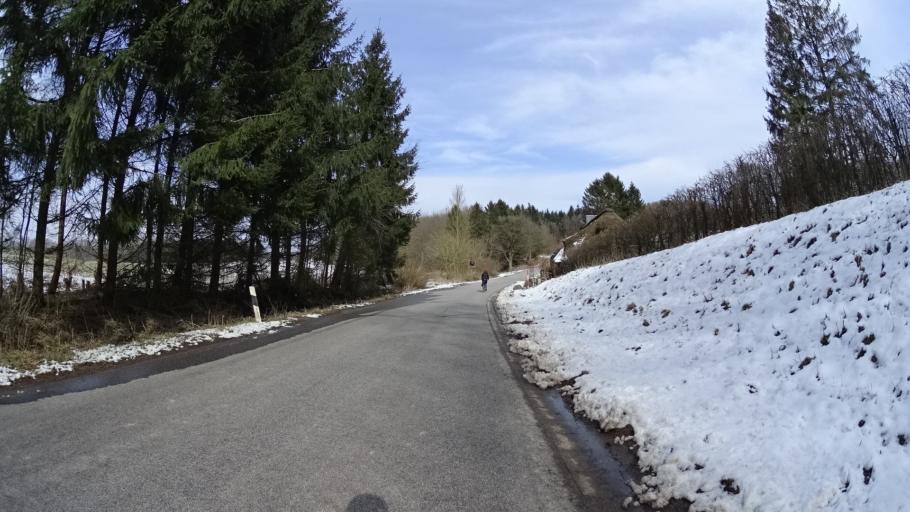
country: DE
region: Schleswig-Holstein
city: Stolpe
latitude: 54.1422
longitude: 10.2310
